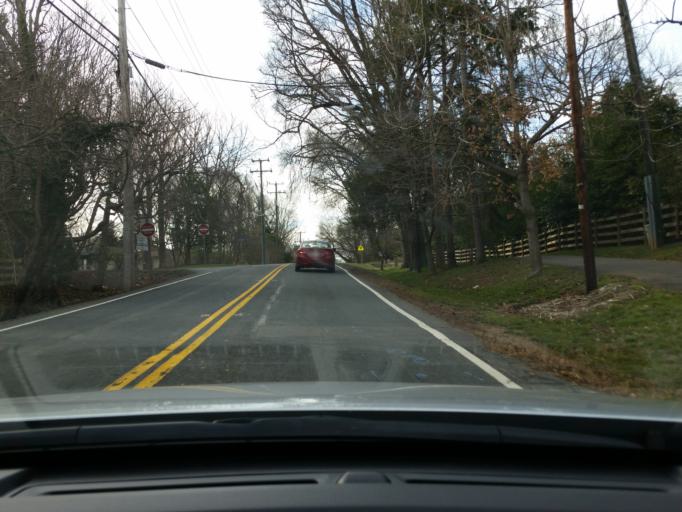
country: US
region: Virginia
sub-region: Fairfax County
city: McLean
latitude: 38.9464
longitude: -77.1584
